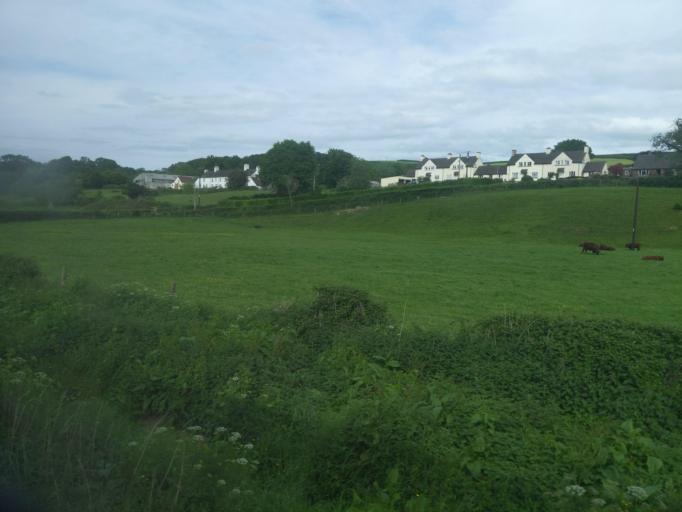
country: GB
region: England
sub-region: Devon
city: Barnstaple
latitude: 50.9919
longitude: -3.9838
